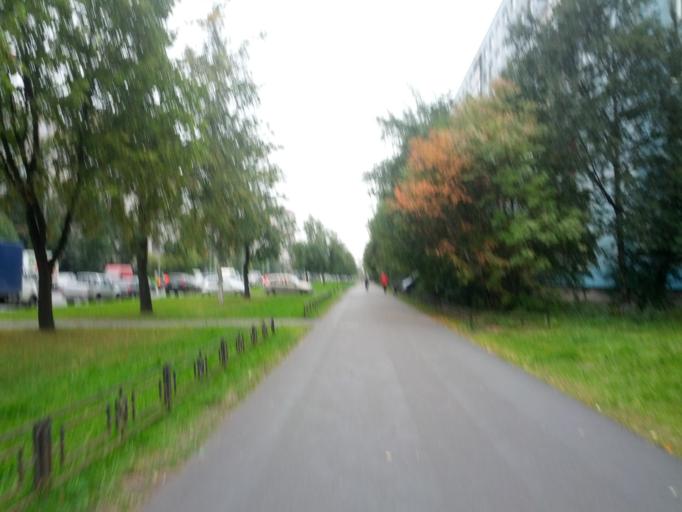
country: RU
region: St.-Petersburg
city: Obukhovo
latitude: 59.8995
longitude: 30.4729
